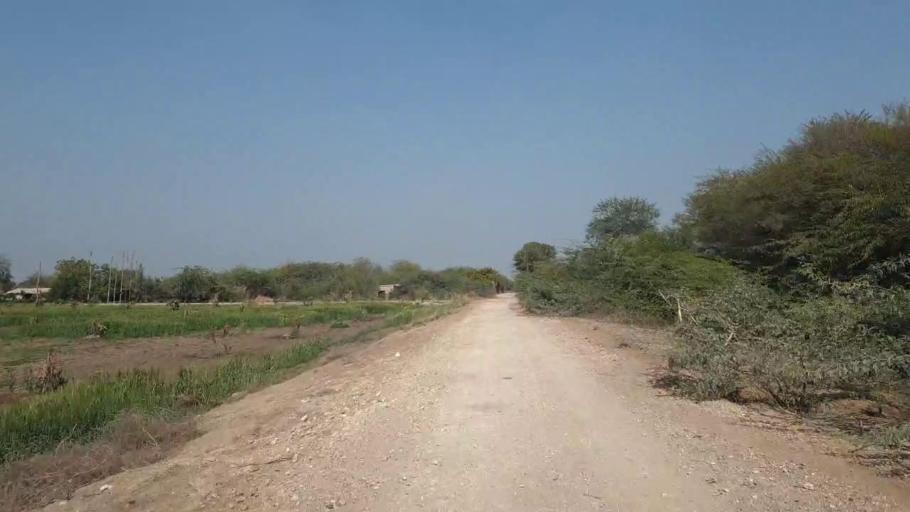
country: PK
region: Sindh
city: Chambar
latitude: 25.4031
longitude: 68.9018
